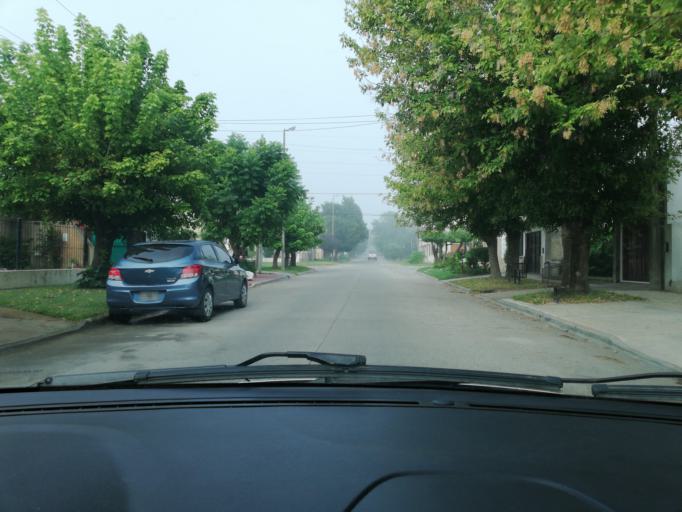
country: AR
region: Buenos Aires
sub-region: Partido de Balcarce
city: Balcarce
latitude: -37.8545
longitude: -58.2465
